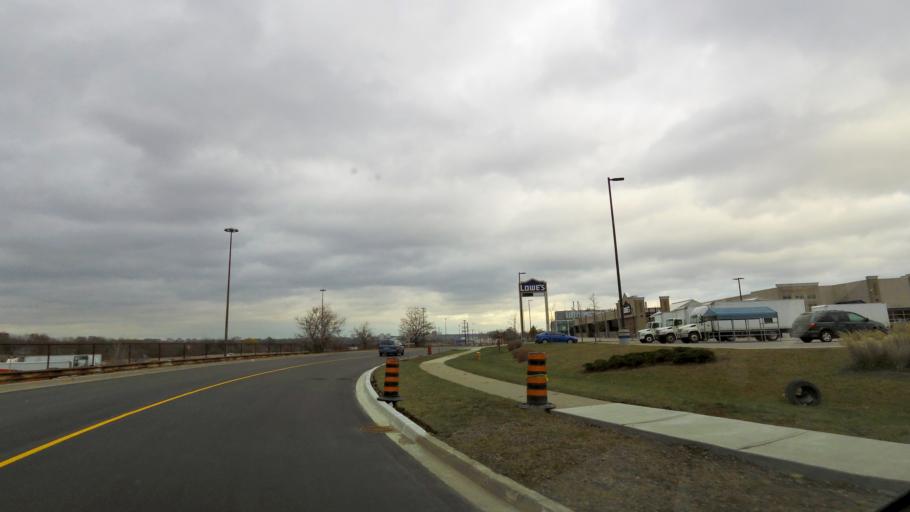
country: CA
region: Ontario
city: Etobicoke
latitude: 43.7094
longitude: -79.5496
